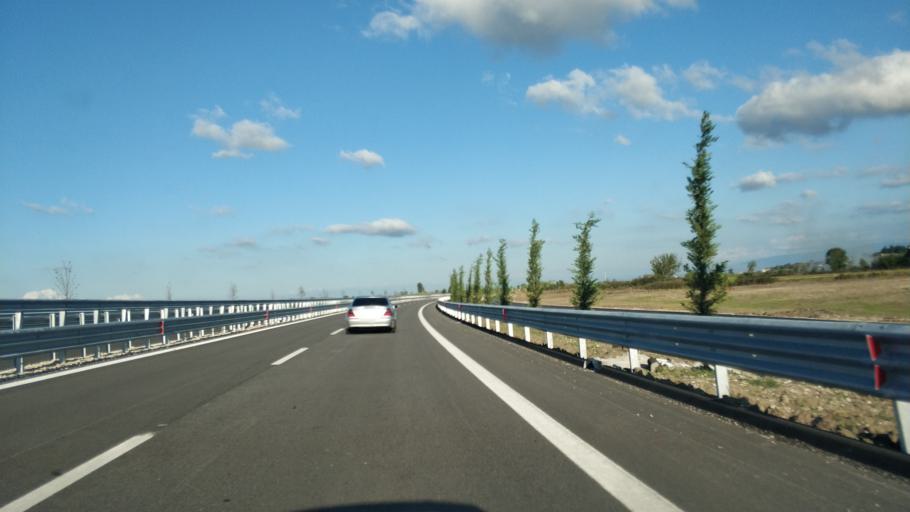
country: AL
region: Fier
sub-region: Rrethi i Fierit
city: Topoje
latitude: 40.7376
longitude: 19.4545
